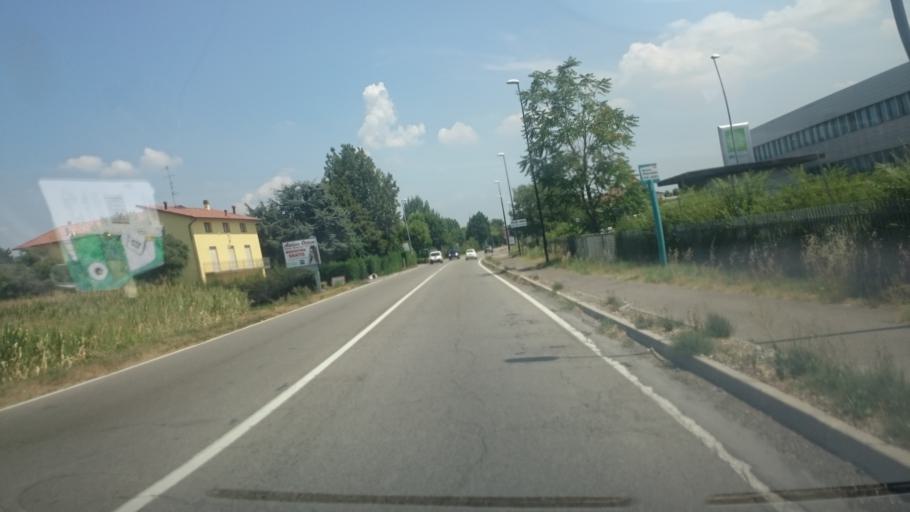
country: IT
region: Emilia-Romagna
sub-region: Provincia di Reggio Emilia
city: Bagno
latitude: 44.6567
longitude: 10.7569
